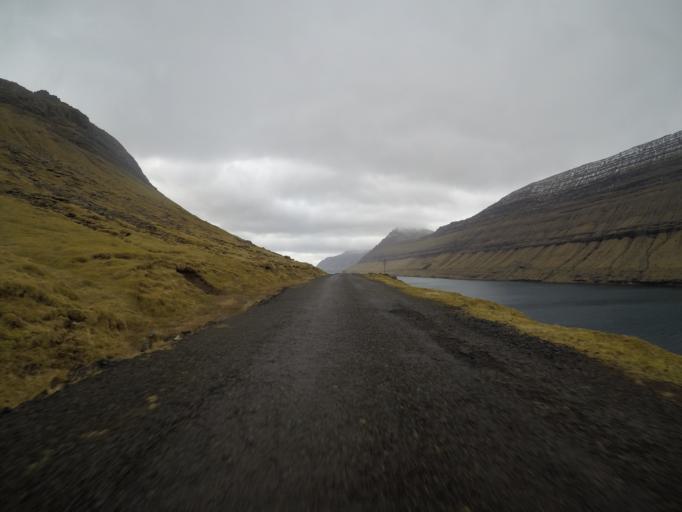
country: FO
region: Nordoyar
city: Klaksvik
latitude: 62.3035
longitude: -6.5381
